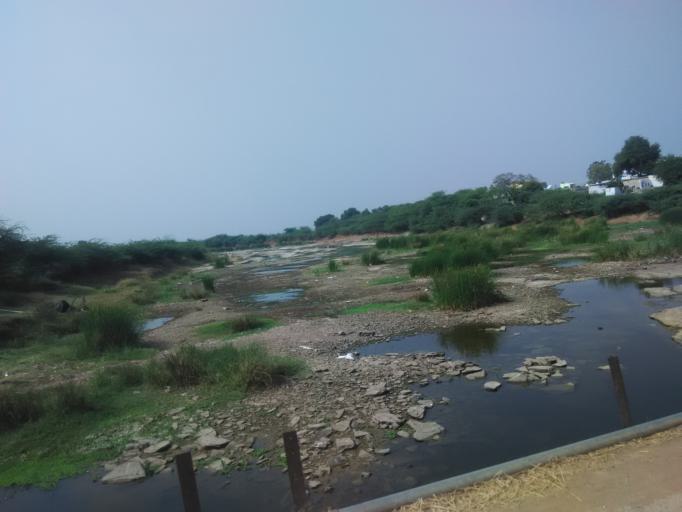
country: IN
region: Andhra Pradesh
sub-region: Kurnool
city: Nandyal
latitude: 15.4489
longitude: 78.4213
